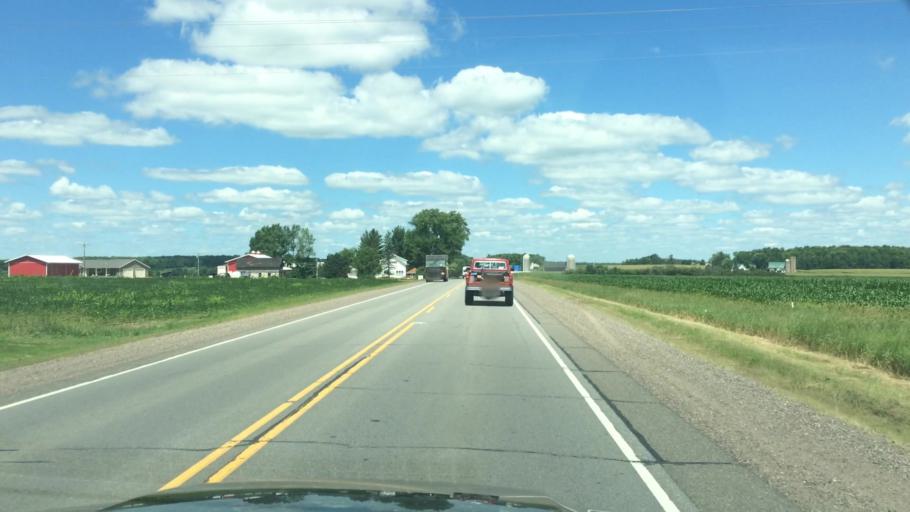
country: US
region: Wisconsin
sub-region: Taylor County
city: Medford
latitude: 45.0840
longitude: -90.3146
